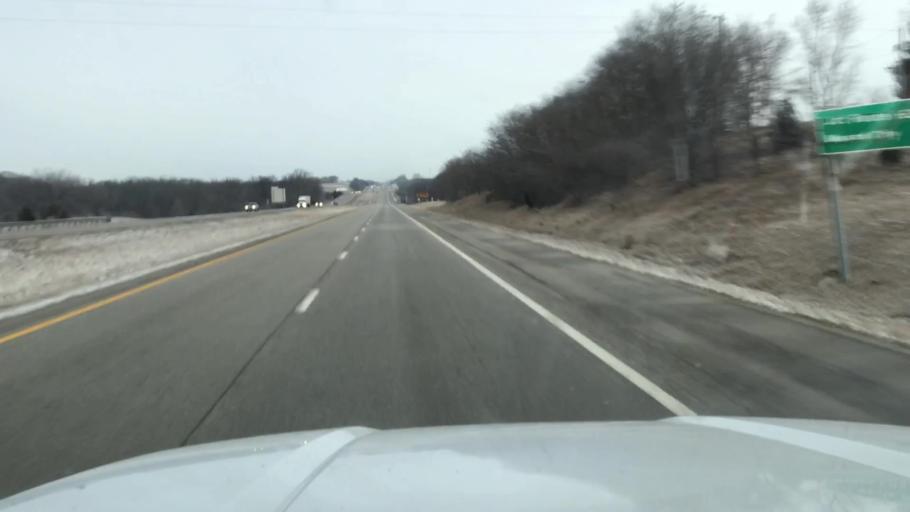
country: US
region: Missouri
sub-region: Andrew County
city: Country Club Village
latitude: 39.8664
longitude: -94.8239
